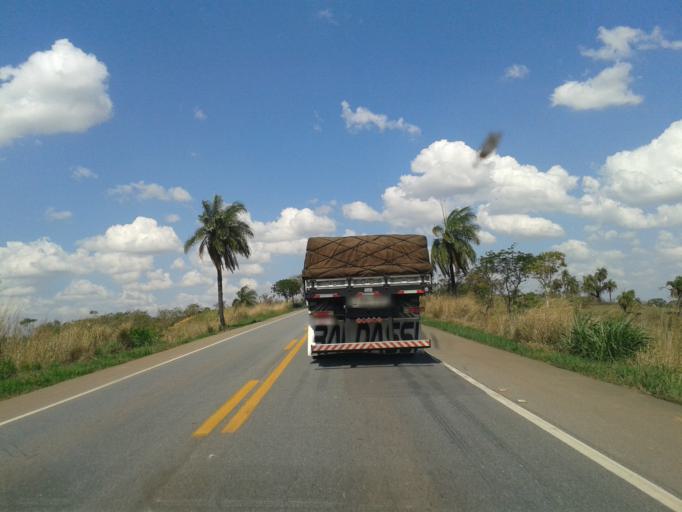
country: BR
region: Minas Gerais
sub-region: Luz
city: Luz
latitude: -19.7412
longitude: -45.8444
